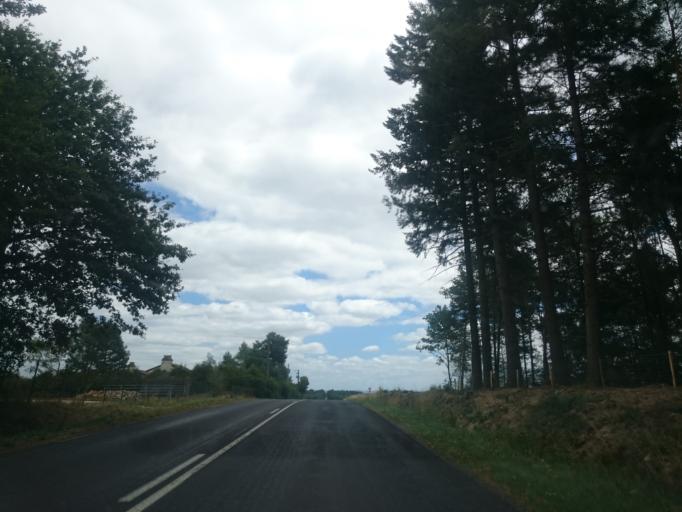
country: FR
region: Auvergne
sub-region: Departement du Cantal
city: Saint-Paul-des-Landes
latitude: 44.9607
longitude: 2.2625
